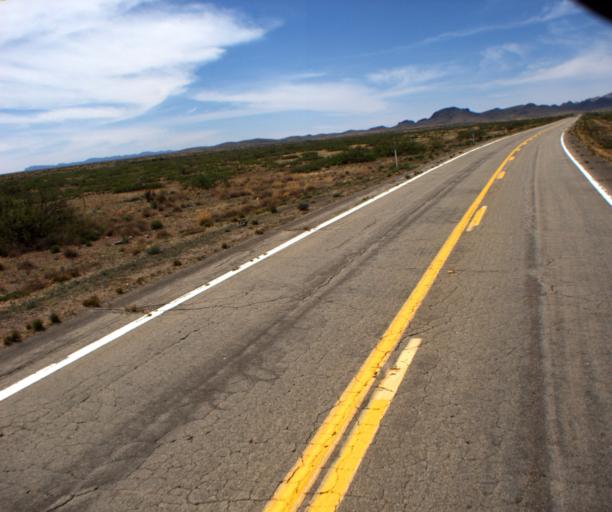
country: US
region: Arizona
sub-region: Cochise County
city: Willcox
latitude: 32.3749
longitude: -109.6415
